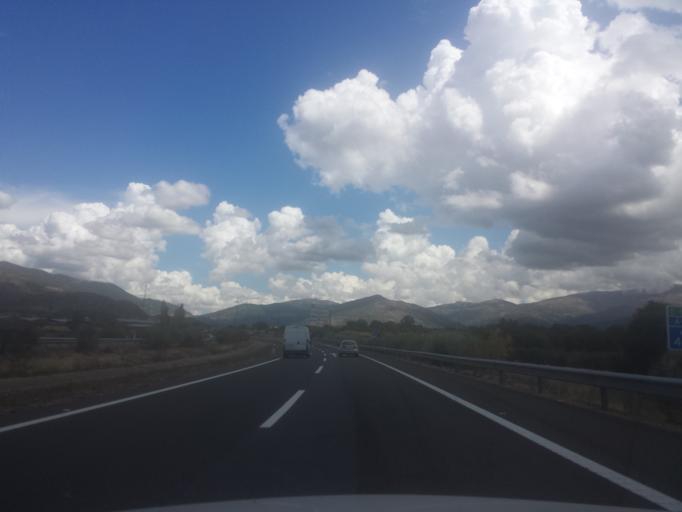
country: ES
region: Extremadura
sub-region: Provincia de Caceres
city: Aldeanueva del Camino
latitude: 40.2587
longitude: -5.9190
